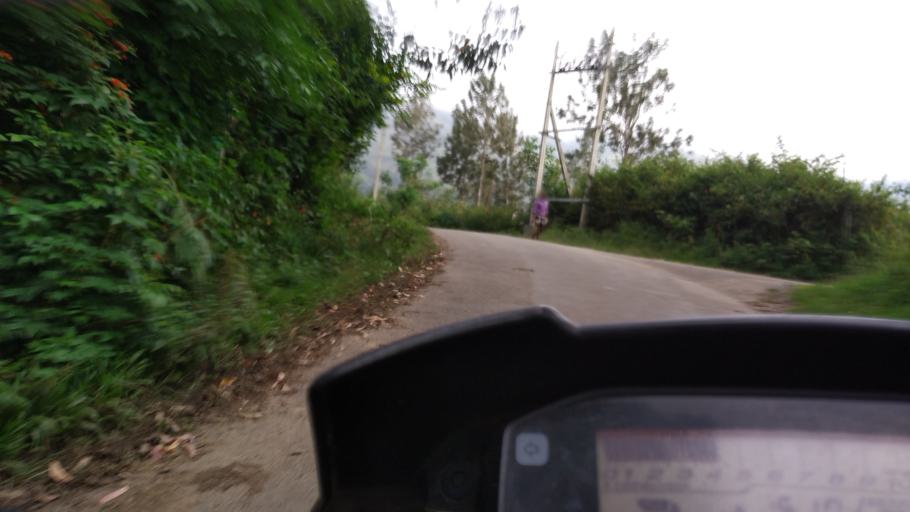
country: IN
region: Tamil Nadu
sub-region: Theni
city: Bodinayakkanur
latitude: 10.0252
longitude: 77.2323
